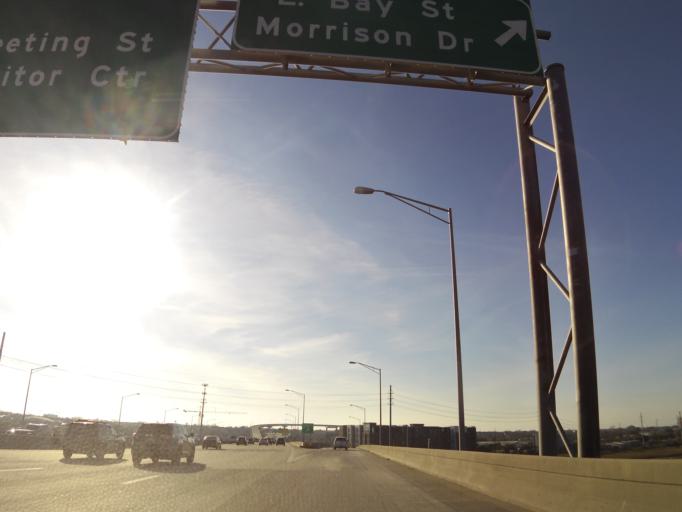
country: US
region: South Carolina
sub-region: Charleston County
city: Charleston
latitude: 32.8052
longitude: -79.9365
